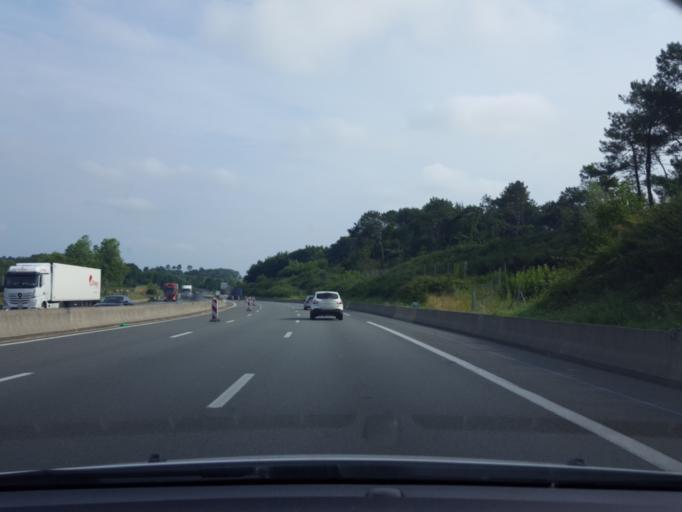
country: FR
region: Aquitaine
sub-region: Departement des Landes
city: Tarnos
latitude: 43.5342
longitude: -1.4311
